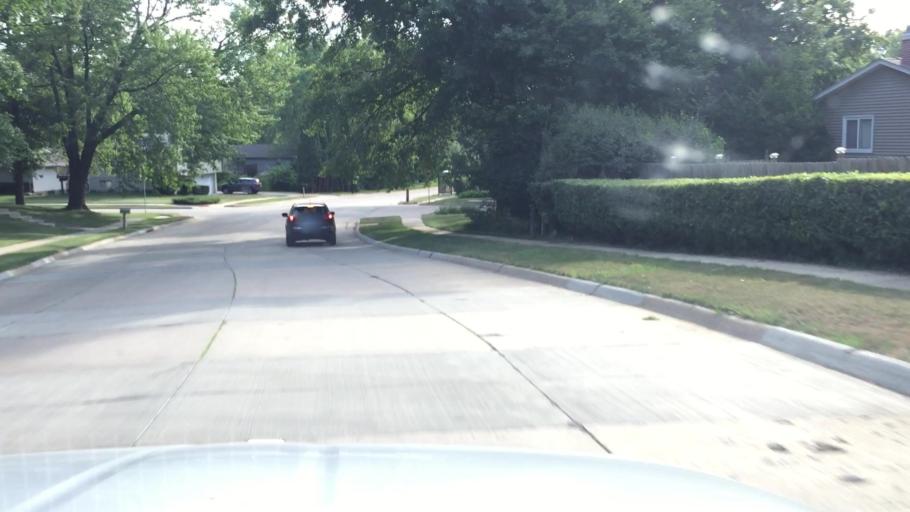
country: US
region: Iowa
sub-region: Johnson County
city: Iowa City
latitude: 41.6609
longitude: -91.4913
